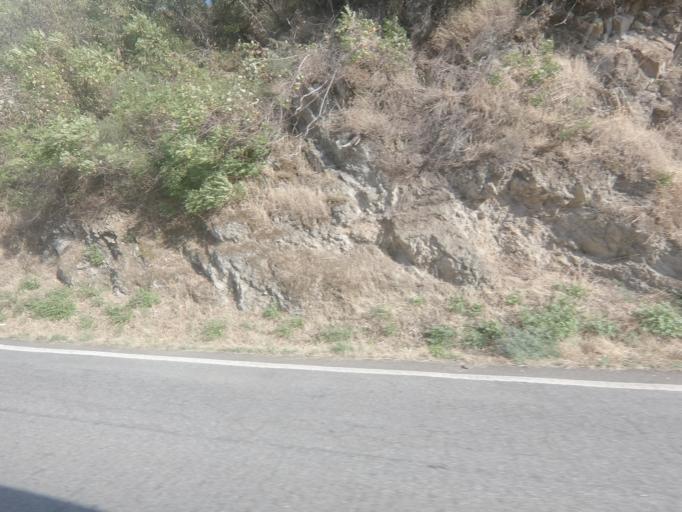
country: PT
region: Vila Real
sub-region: Sabrosa
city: Vilela
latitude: 41.1873
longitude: -7.5469
